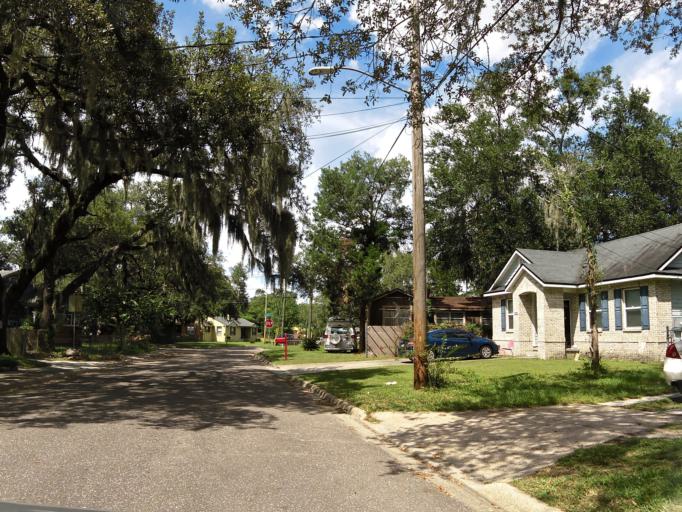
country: US
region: Florida
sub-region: Duval County
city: Jacksonville
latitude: 30.3872
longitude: -81.6452
